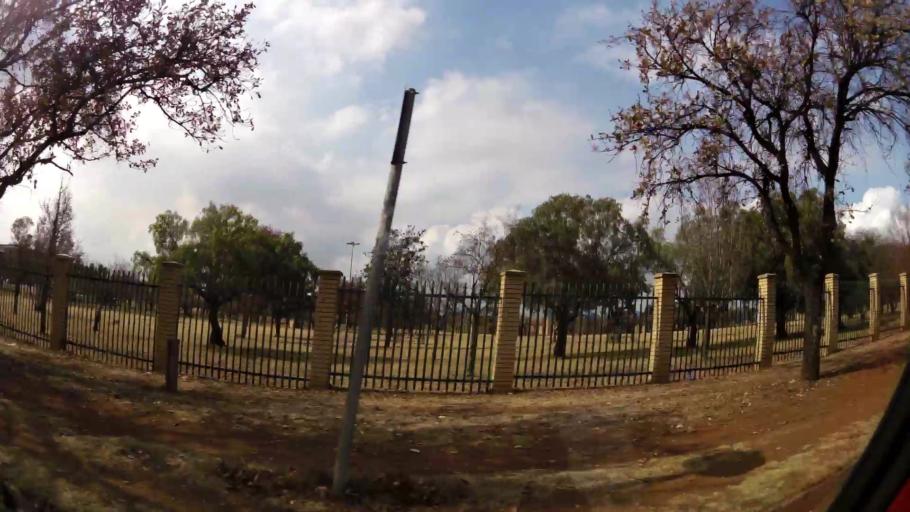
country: ZA
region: Gauteng
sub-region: Sedibeng District Municipality
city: Vanderbijlpark
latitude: -26.7143
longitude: 27.8626
